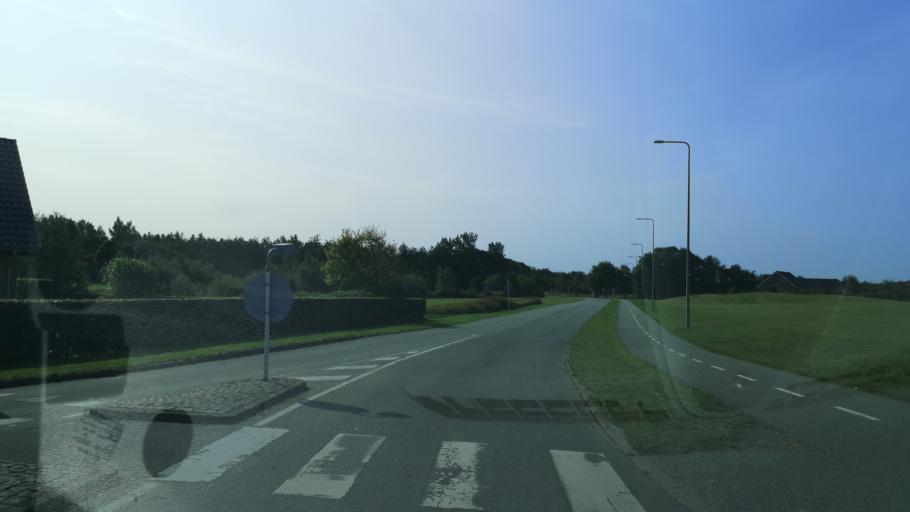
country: DK
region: Central Jutland
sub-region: Ringkobing-Skjern Kommune
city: Videbaek
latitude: 56.0793
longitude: 8.6171
